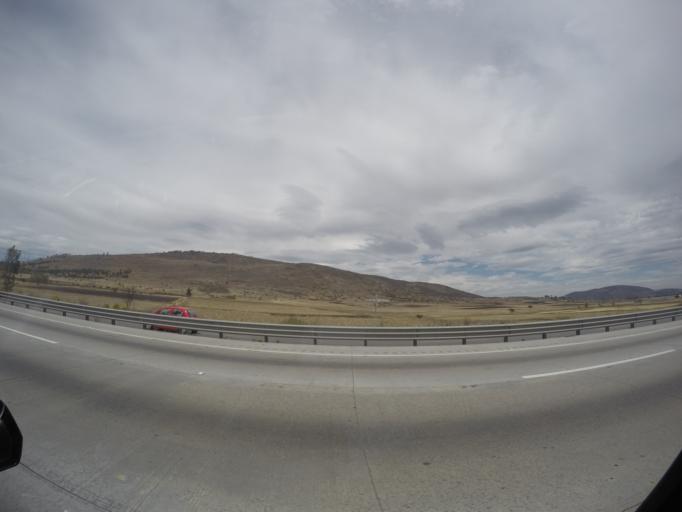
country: MX
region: Mexico
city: San Francisco Soyaniquilpan
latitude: 19.9991
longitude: -99.4910
